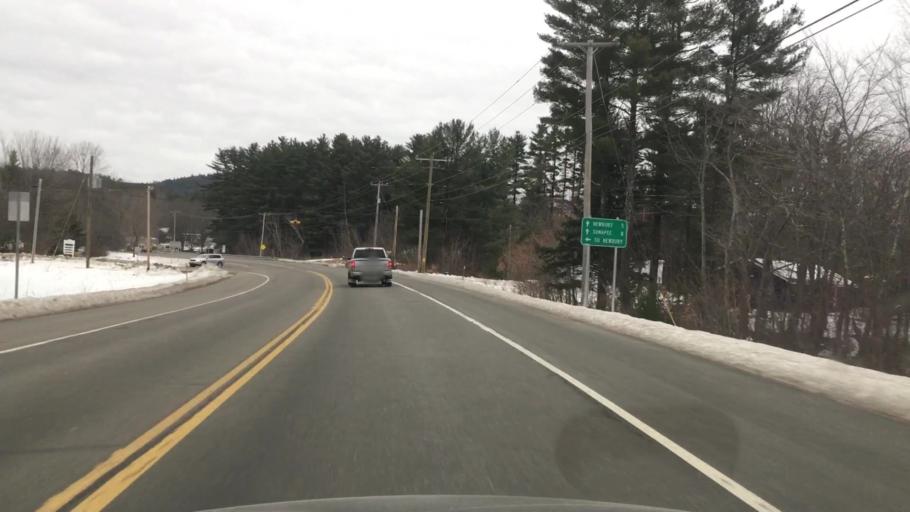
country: US
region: New Hampshire
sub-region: Merrimack County
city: Newbury
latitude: 43.2946
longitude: -71.9945
